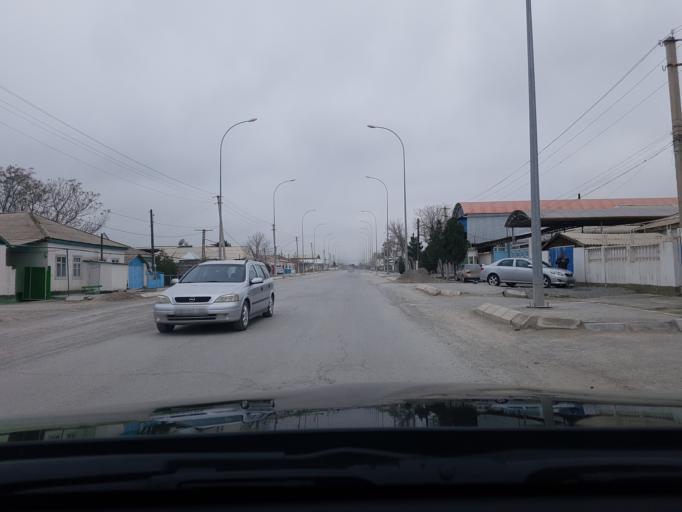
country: TM
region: Ahal
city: Abadan
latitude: 38.1569
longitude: 57.9584
